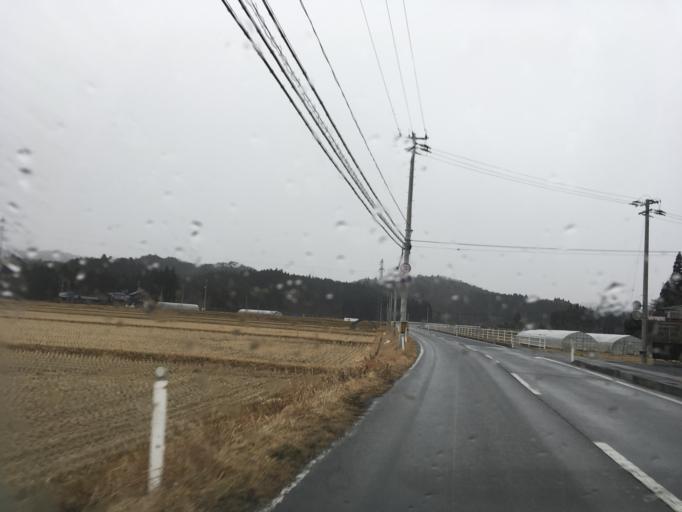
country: JP
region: Iwate
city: Ichinoseki
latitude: 38.8438
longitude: 140.9593
